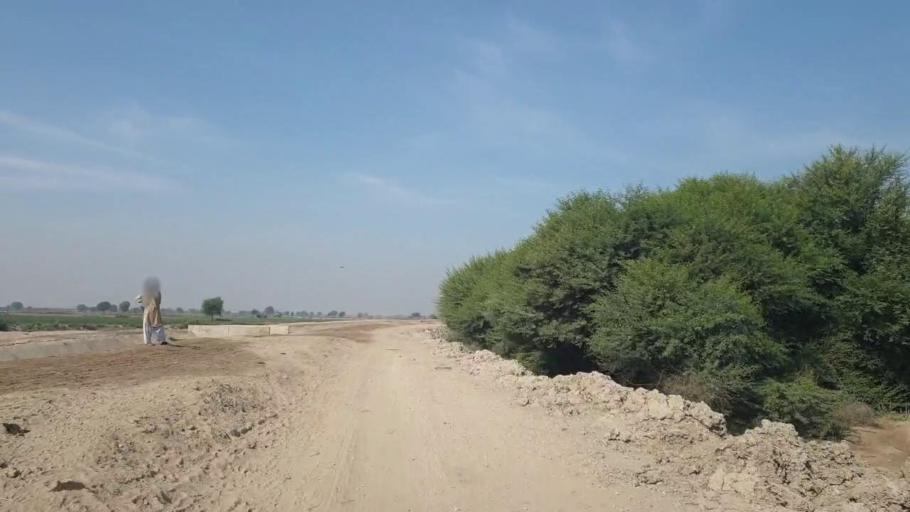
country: PK
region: Sindh
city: Matiari
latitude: 25.6834
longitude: 68.3361
